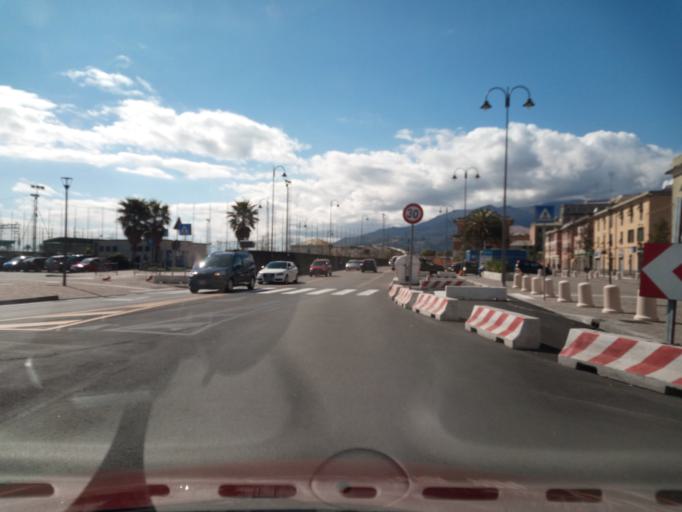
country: IT
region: Liguria
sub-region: Provincia di Genova
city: Mele
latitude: 44.4269
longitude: 8.7868
